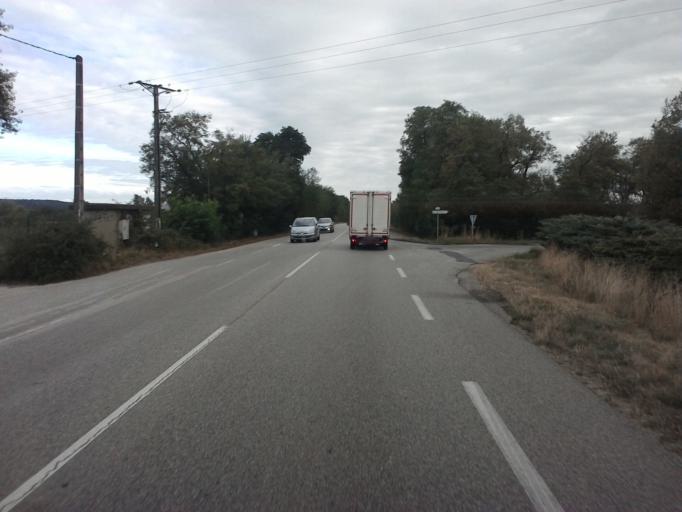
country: FR
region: Rhone-Alpes
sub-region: Departement de l'Ain
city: Ambronay
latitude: 46.0155
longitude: 5.3401
